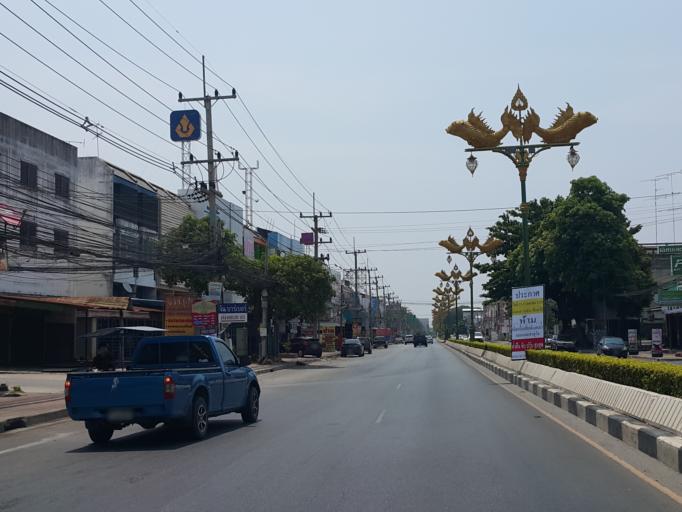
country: TH
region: Kanchanaburi
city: Kanchanaburi
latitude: 14.0363
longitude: 99.5210
